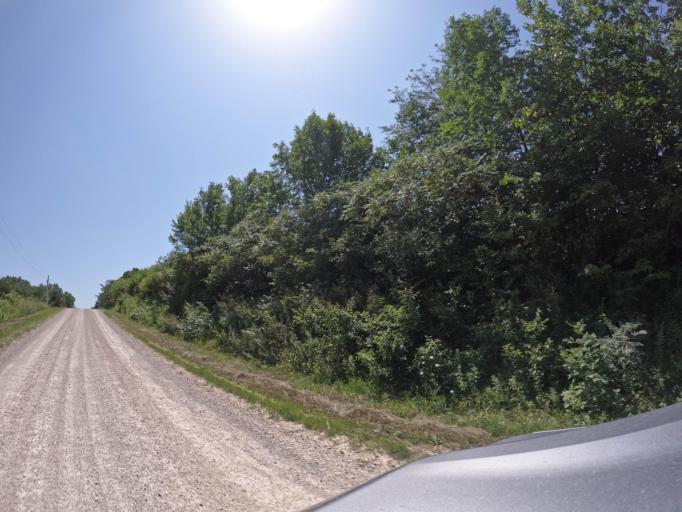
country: US
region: Iowa
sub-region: Henry County
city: Mount Pleasant
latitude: 40.9880
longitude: -91.6362
